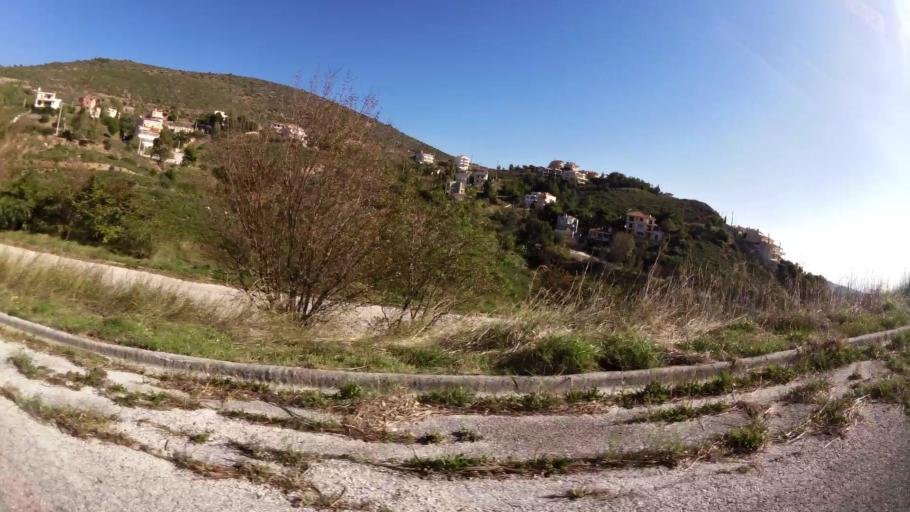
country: GR
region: Attica
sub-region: Nomarchia Anatolikis Attikis
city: Dhrafi
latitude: 38.0426
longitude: 23.8960
